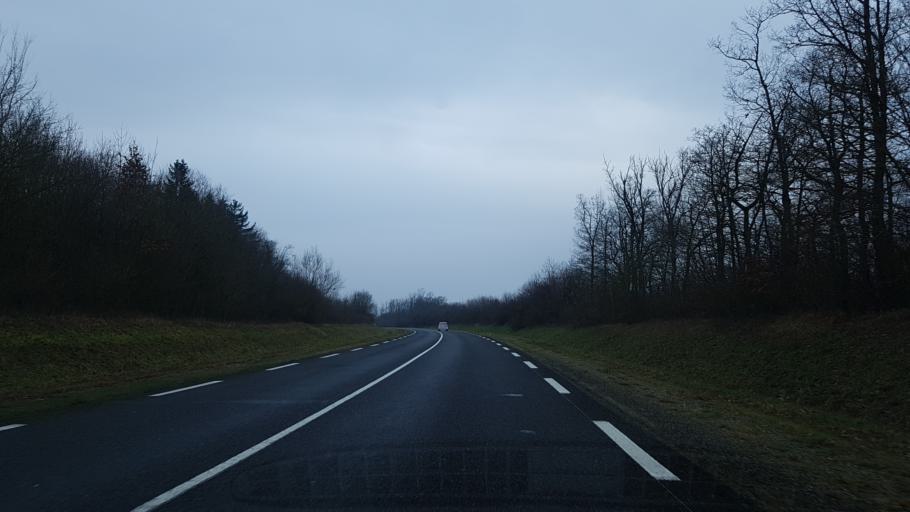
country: FR
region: Lorraine
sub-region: Departement de la Moselle
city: Gros-Rederching
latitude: 49.1018
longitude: 7.2316
